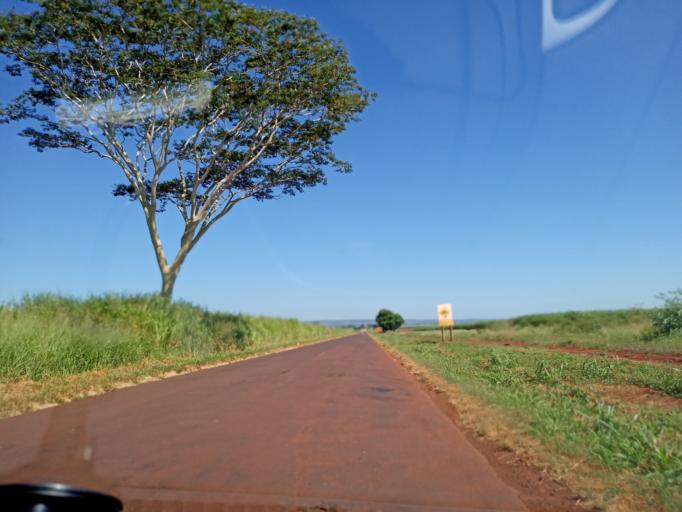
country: BR
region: Goias
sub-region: Itumbiara
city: Itumbiara
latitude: -18.4524
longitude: -49.1567
